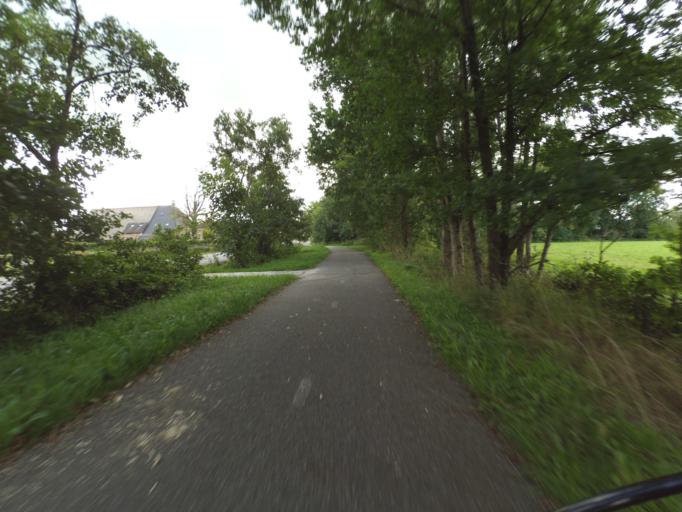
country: NL
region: Friesland
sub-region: Gemeente Tytsjerksteradiel
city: Burgum
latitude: 53.2058
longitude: 5.9769
